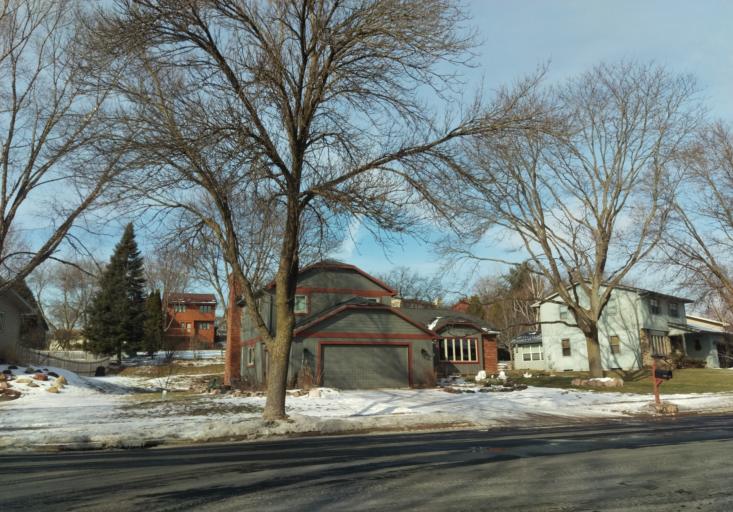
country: US
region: Wisconsin
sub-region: Dane County
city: Middleton
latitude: 43.0884
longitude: -89.5158
